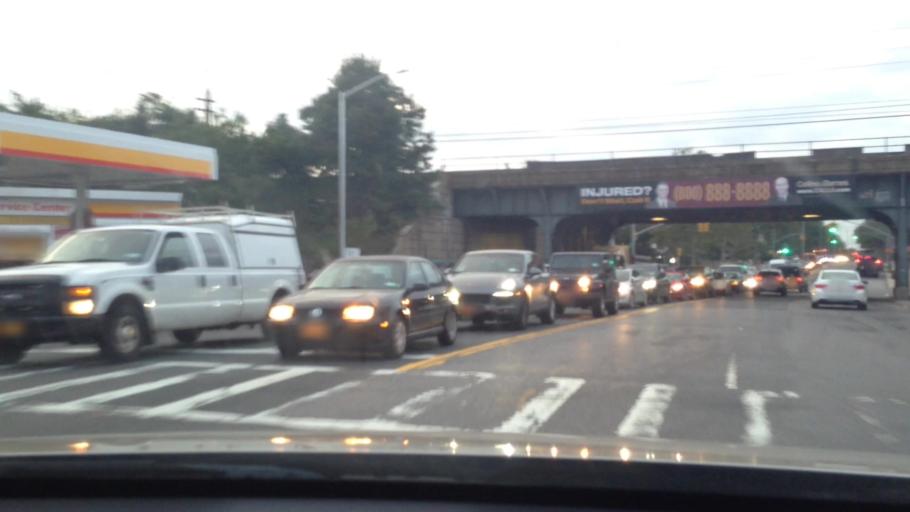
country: US
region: New York
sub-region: Nassau County
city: Bellerose Terrace
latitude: 40.7138
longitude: -73.7540
